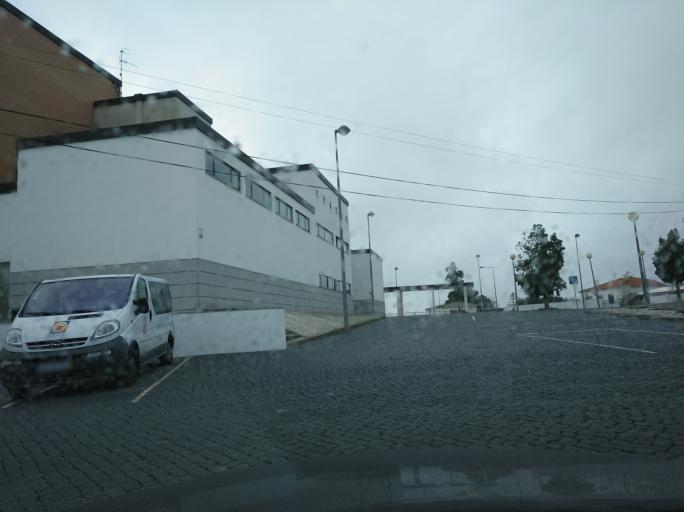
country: PT
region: Portalegre
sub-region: Campo Maior
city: Campo Maior
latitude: 39.0205
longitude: -7.0665
